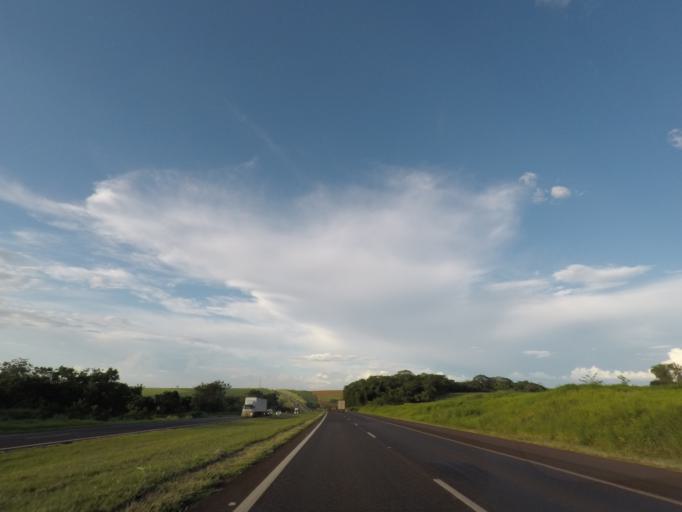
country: BR
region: Sao Paulo
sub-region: Ituverava
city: Ituverava
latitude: -20.2919
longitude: -47.7981
